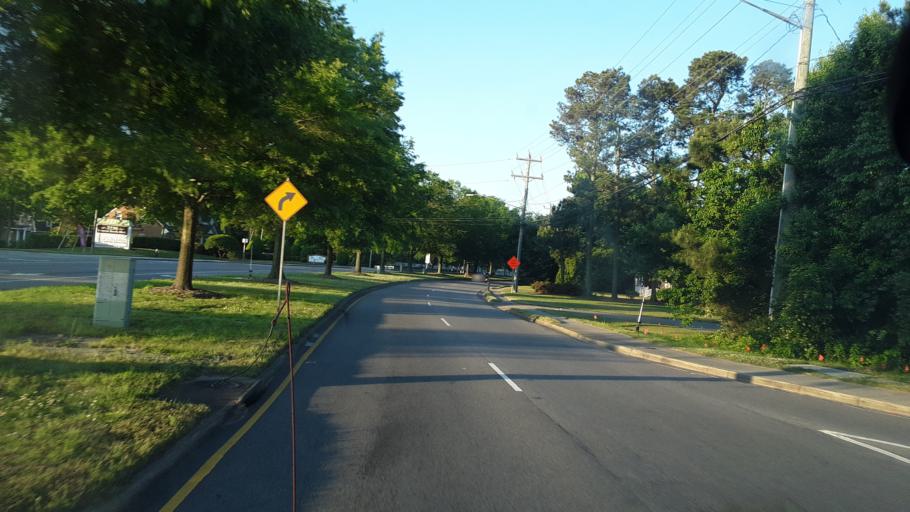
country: US
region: Virginia
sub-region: City of Virginia Beach
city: Virginia Beach
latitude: 36.7634
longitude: -76.0157
